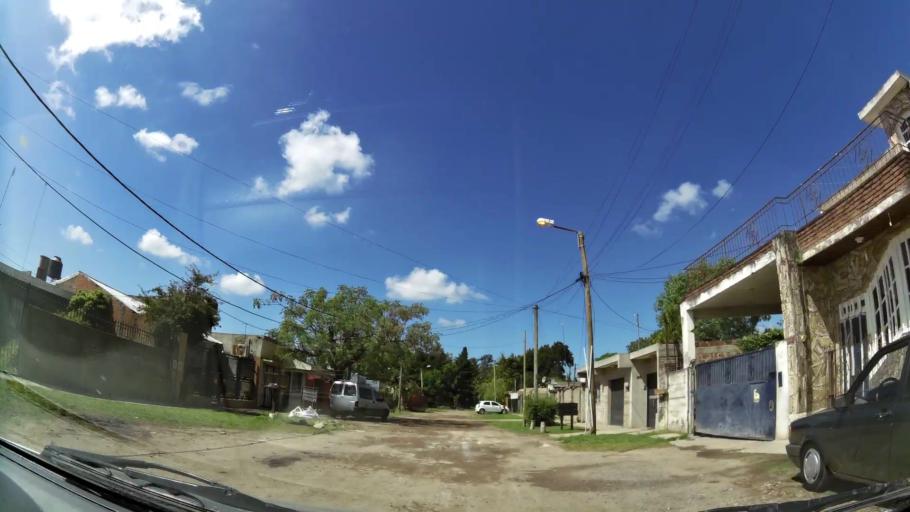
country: AR
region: Buenos Aires
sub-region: Partido de Quilmes
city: Quilmes
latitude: -34.8232
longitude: -58.2688
